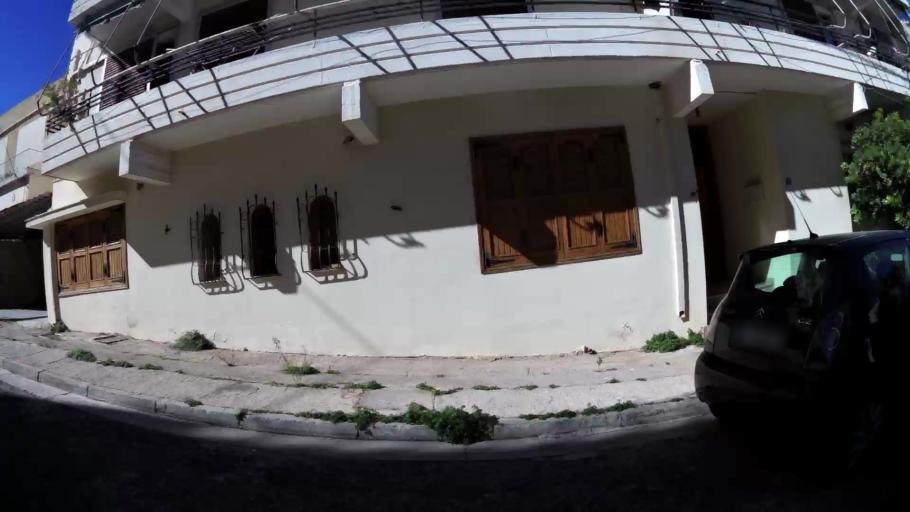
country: GR
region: Attica
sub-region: Nomarchia Anatolikis Attikis
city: Koropi
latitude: 37.9040
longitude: 23.8767
